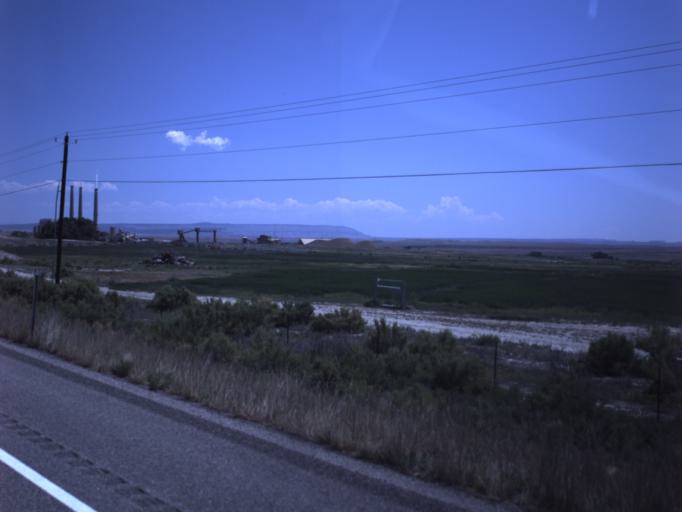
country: US
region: Utah
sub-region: Emery County
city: Orangeville
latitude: 39.1647
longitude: -111.0652
